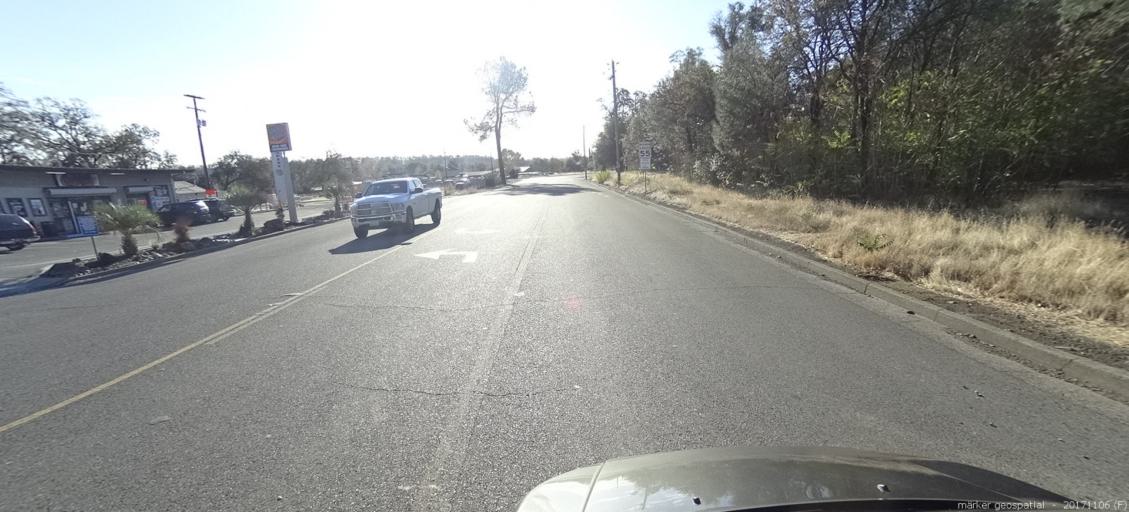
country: US
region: California
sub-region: Shasta County
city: Bella Vista
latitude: 40.6379
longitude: -122.2418
